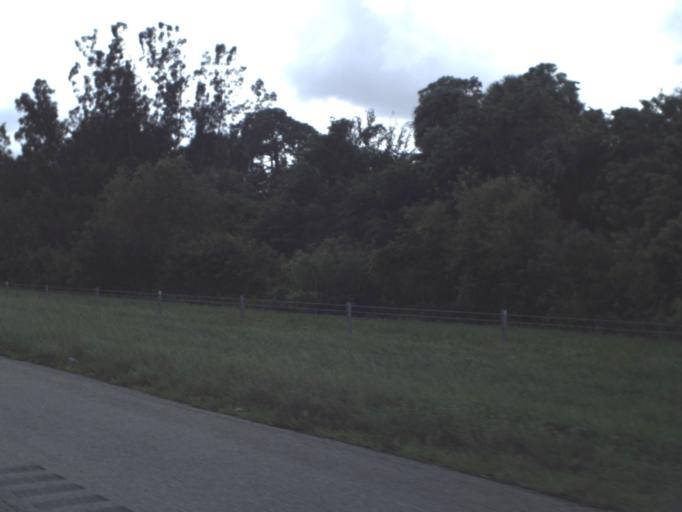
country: US
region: Florida
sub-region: Palm Beach County
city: Palm Beach Gardens
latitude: 26.8609
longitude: -80.1293
